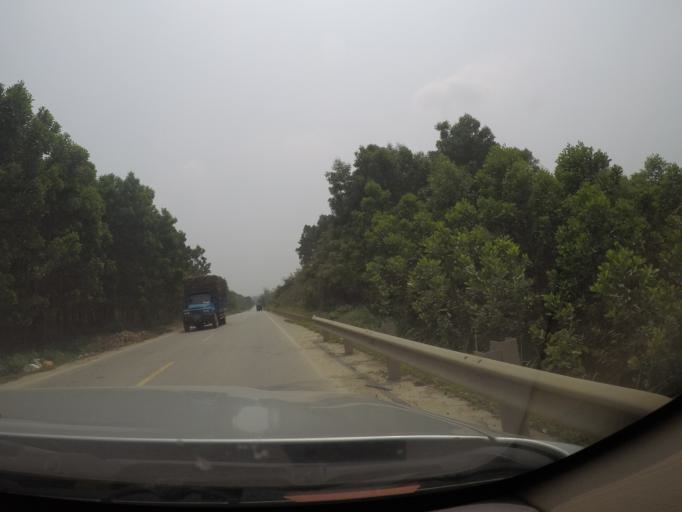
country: VN
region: Thanh Hoa
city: Thi Tran Yen Cat
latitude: 19.7497
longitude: 105.4223
